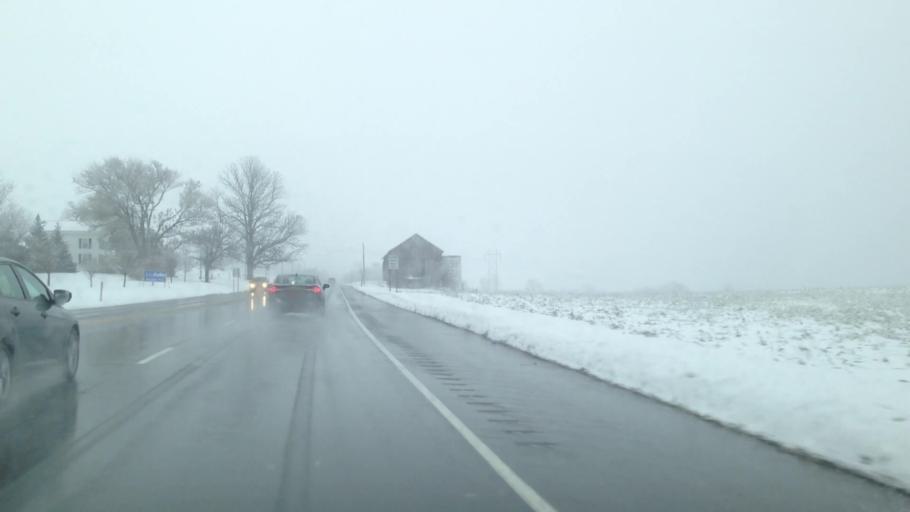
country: US
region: New York
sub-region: Onondaga County
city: Peru
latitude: 43.0371
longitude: -76.3949
